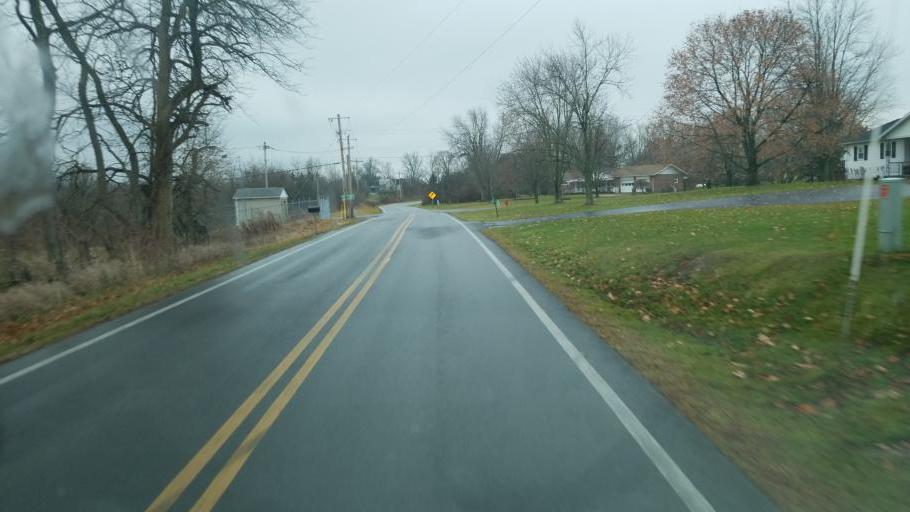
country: US
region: Ohio
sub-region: Delaware County
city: Ashley
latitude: 40.3957
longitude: -82.9477
